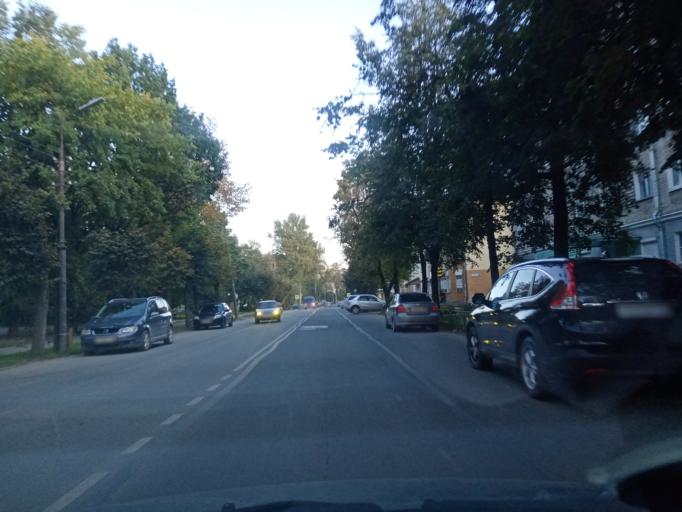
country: RU
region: Pskov
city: Pskov
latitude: 57.8068
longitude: 28.3409
